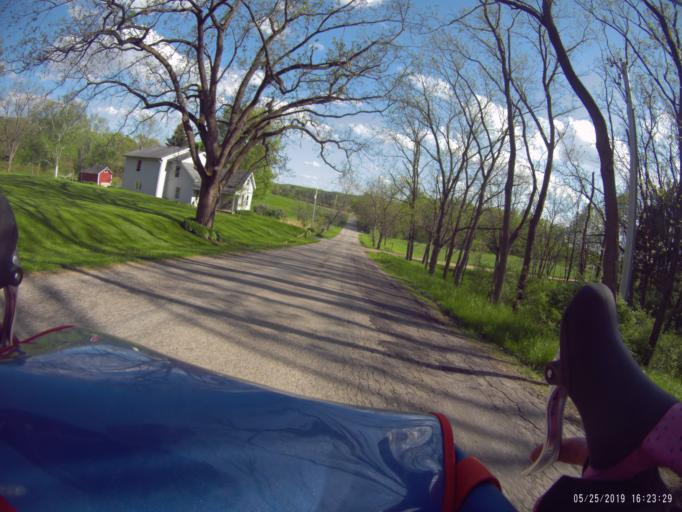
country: US
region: Wisconsin
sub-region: Dane County
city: Mount Horeb
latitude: 42.9581
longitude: -89.7014
